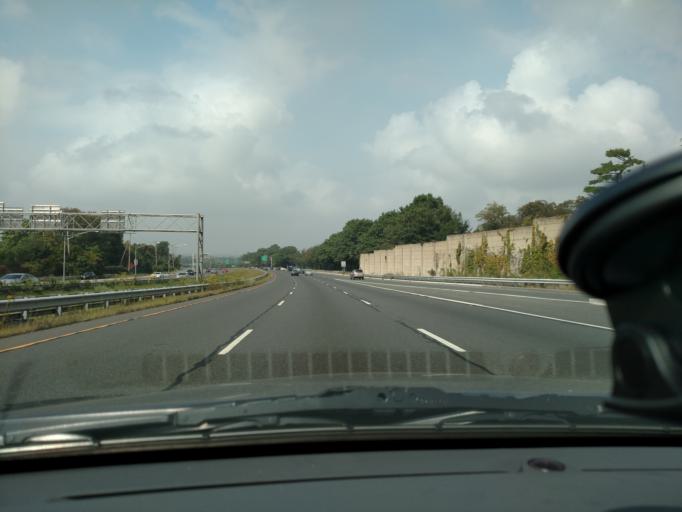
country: US
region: New Jersey
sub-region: Union County
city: Summit
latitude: 40.7350
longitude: -74.3566
